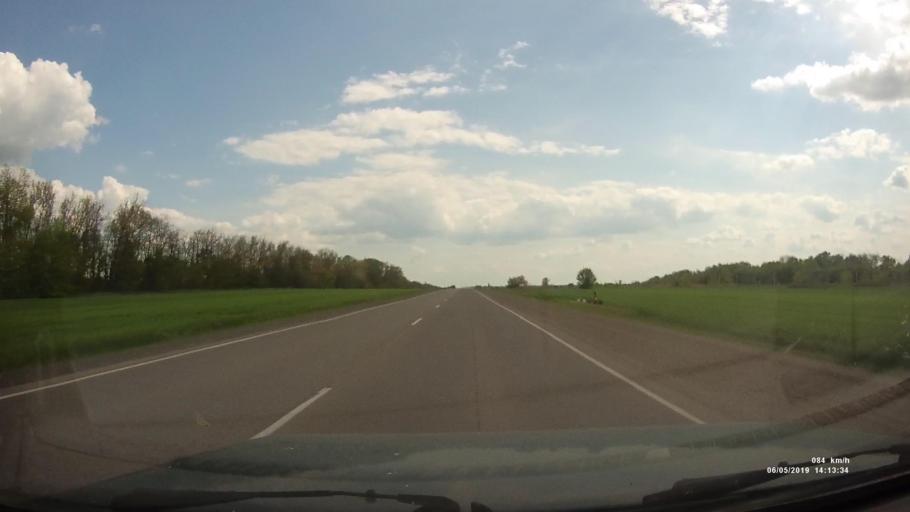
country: RU
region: Rostov
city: Kamenolomni
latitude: 47.6591
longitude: 40.2931
